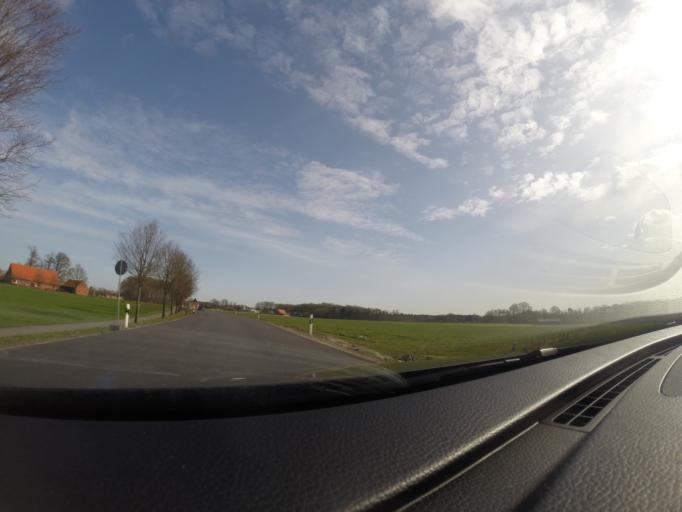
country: DE
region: North Rhine-Westphalia
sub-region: Regierungsbezirk Munster
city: Legden
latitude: 52.0492
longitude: 7.0681
